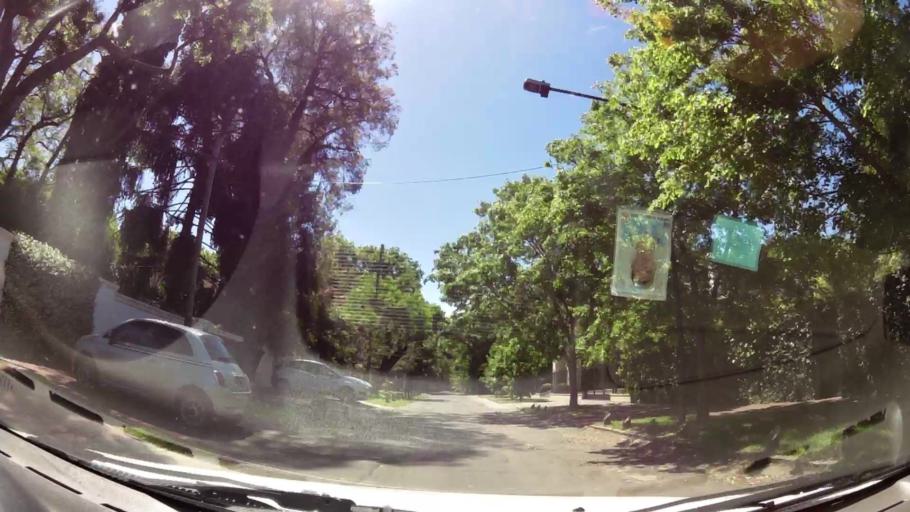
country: AR
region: Buenos Aires
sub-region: Partido de San Isidro
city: San Isidro
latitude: -34.4766
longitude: -58.4898
